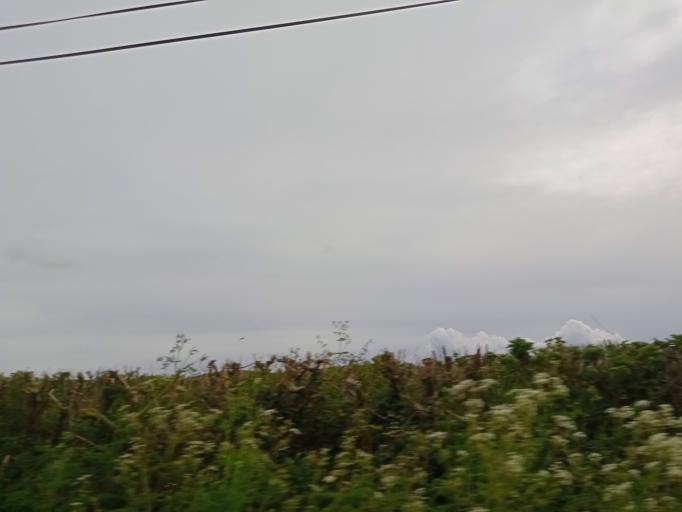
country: IE
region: Leinster
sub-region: Laois
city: Rathdowney
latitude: 52.7078
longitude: -7.4886
